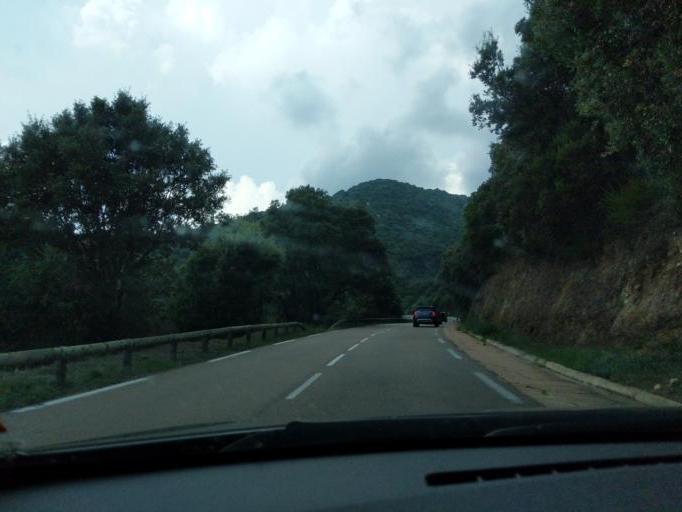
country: FR
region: Corsica
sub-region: Departement de la Corse-du-Sud
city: Sartene
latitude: 41.5789
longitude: 8.9524
